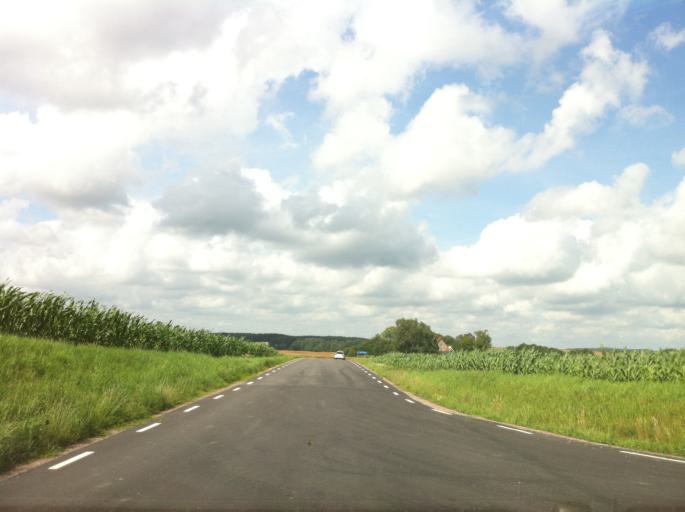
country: SE
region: Skane
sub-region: Trelleborgs Kommun
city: Anderslov
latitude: 55.4491
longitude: 13.3639
